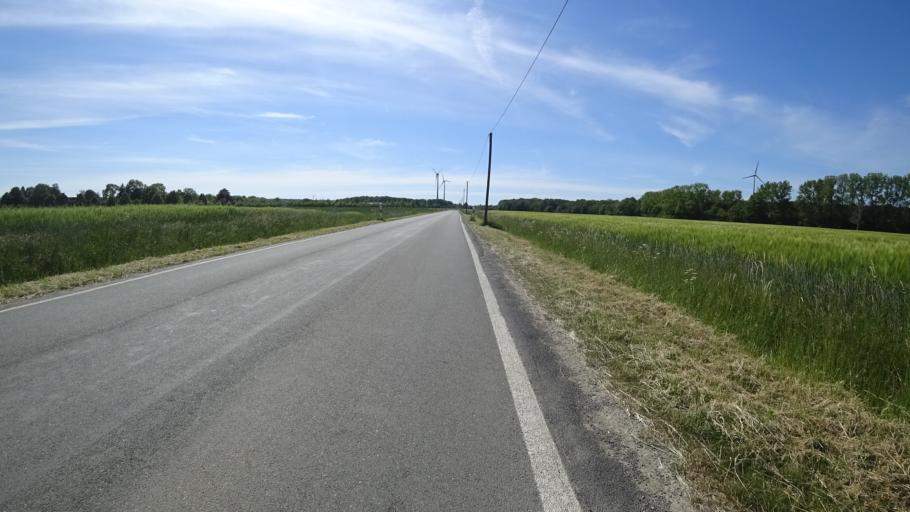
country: DE
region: North Rhine-Westphalia
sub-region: Regierungsbezirk Detmold
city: Rheda-Wiedenbruck
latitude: 51.8244
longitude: 8.2371
